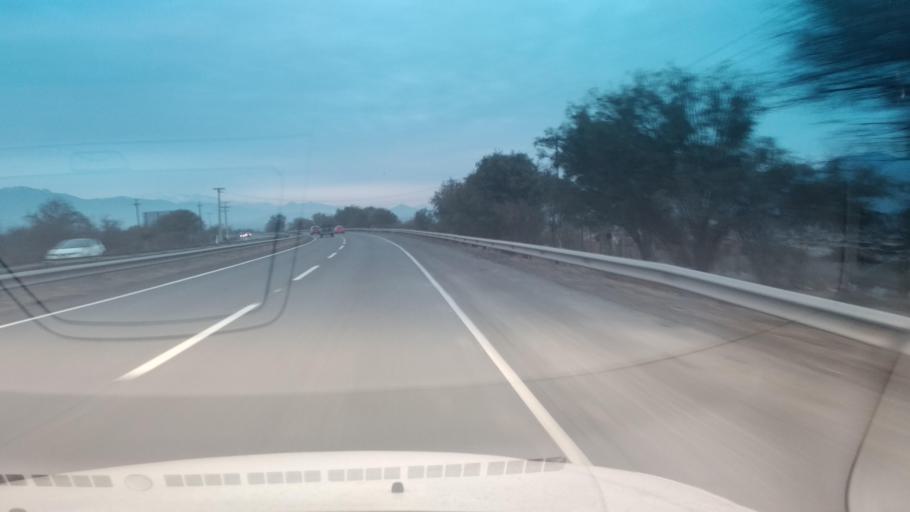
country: CL
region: Santiago Metropolitan
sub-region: Provincia de Chacabuco
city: Chicureo Abajo
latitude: -33.1071
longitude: -70.6897
